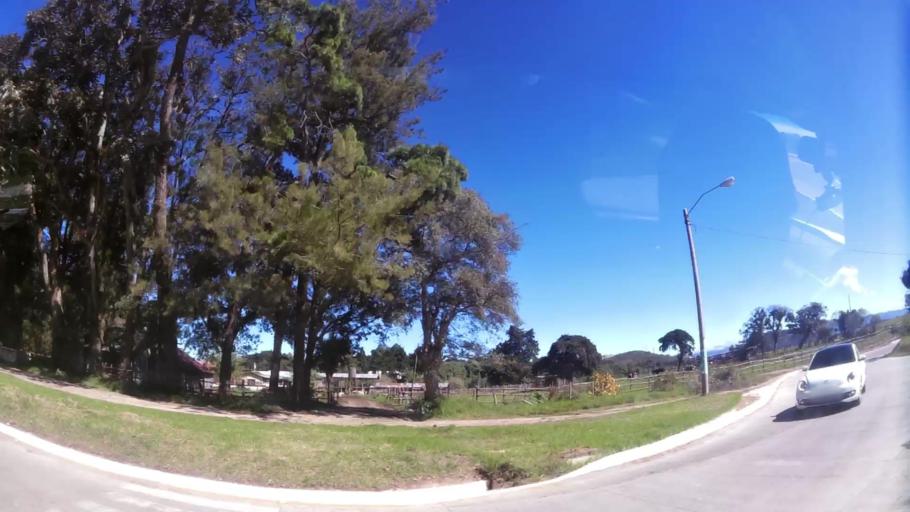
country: GT
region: Guatemala
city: San Jose Pinula
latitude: 14.5199
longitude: -90.4544
